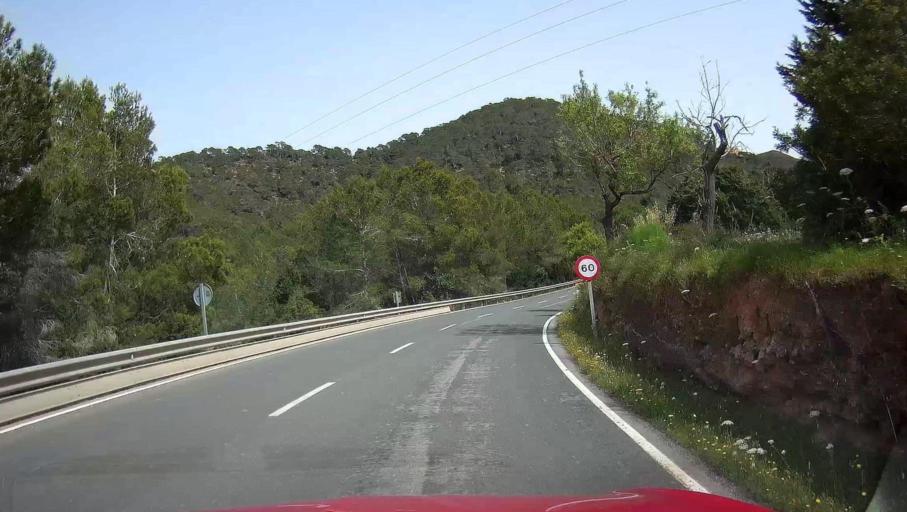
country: ES
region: Balearic Islands
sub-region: Illes Balears
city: Sant Joan de Labritja
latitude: 39.1000
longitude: 1.5092
